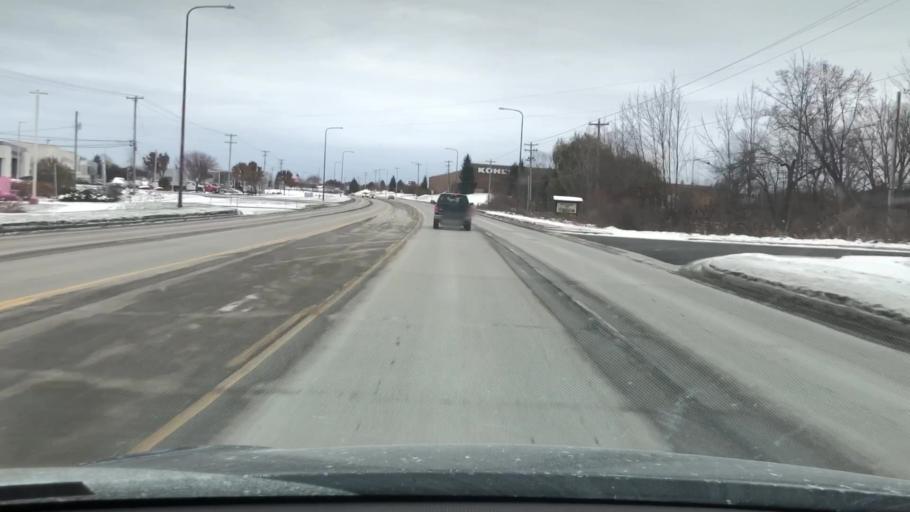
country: US
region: Michigan
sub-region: Grand Traverse County
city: Traverse City
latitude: 44.7382
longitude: -85.6452
